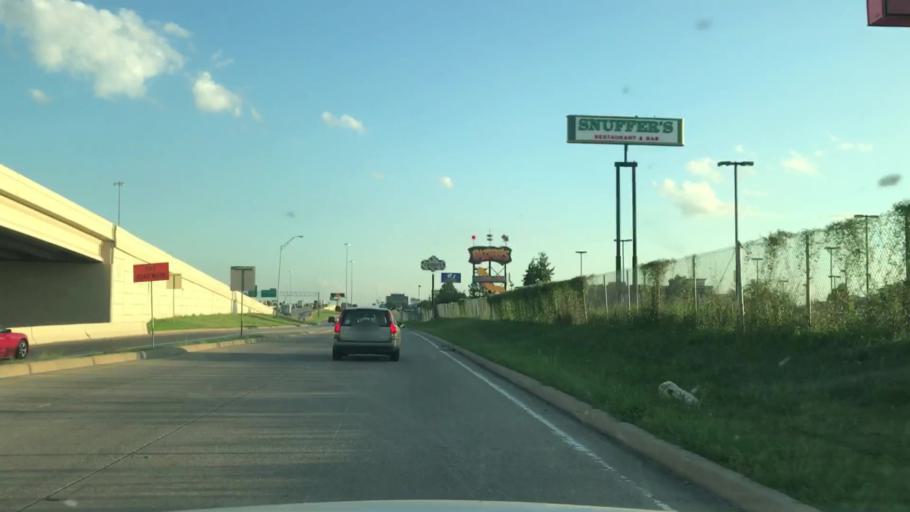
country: US
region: Texas
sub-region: Dallas County
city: Mesquite
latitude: 32.8166
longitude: -96.6291
